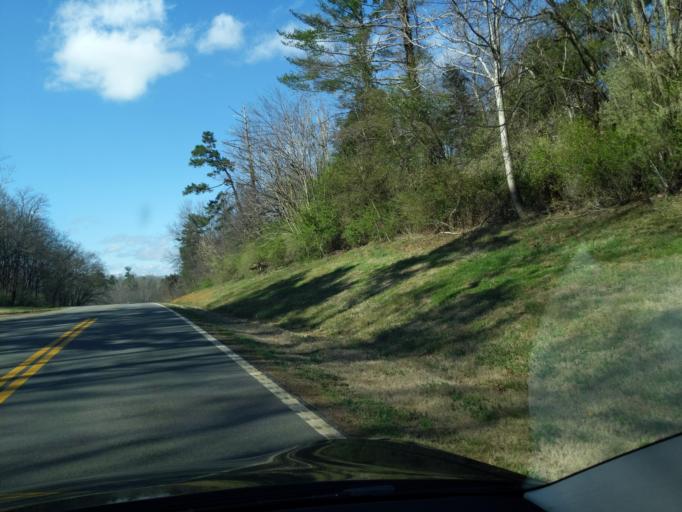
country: US
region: Tennessee
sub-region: Sevier County
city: Sevierville
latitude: 35.9678
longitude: -83.5429
